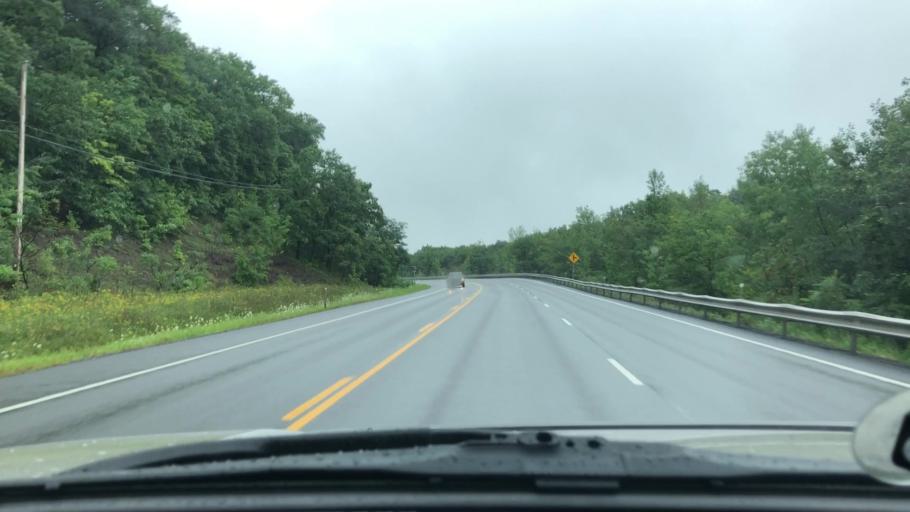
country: US
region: New York
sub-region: Greene County
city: Cairo
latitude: 42.3358
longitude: -74.1157
